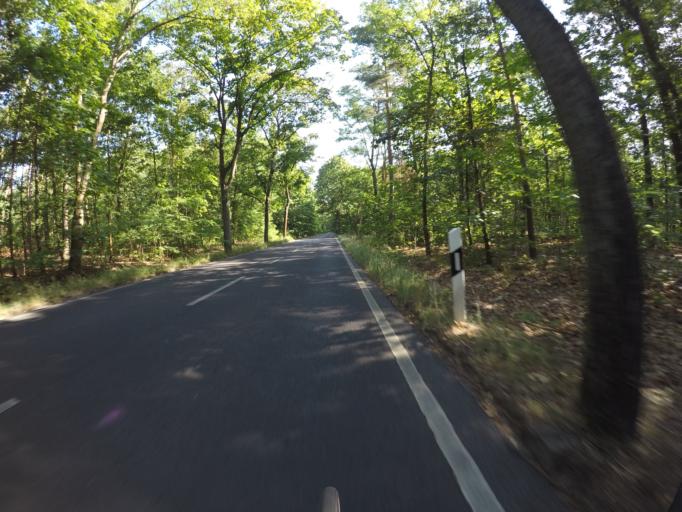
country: DE
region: Berlin
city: Schmockwitz
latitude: 52.3702
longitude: 13.6572
